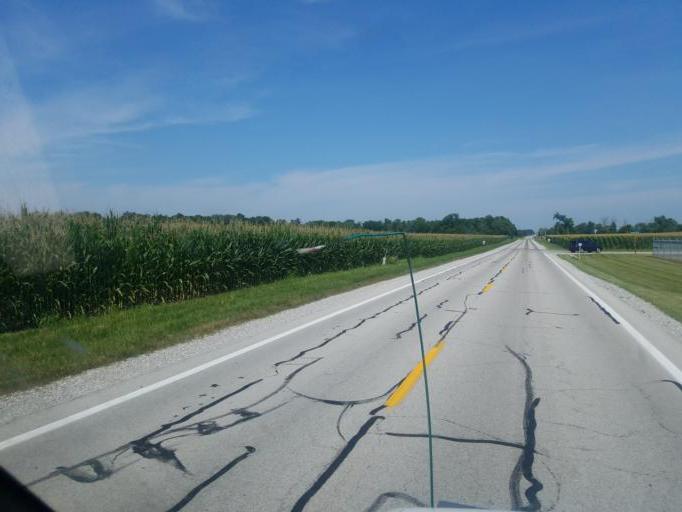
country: US
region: Ohio
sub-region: Shelby County
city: Botkins
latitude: 40.4962
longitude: -84.2863
